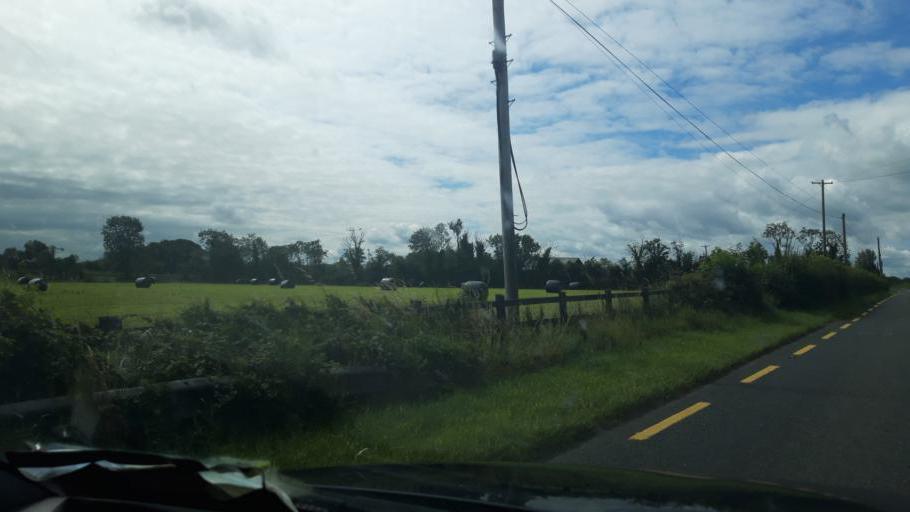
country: IE
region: Leinster
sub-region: Kilkenny
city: Callan
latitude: 52.5294
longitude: -7.4121
